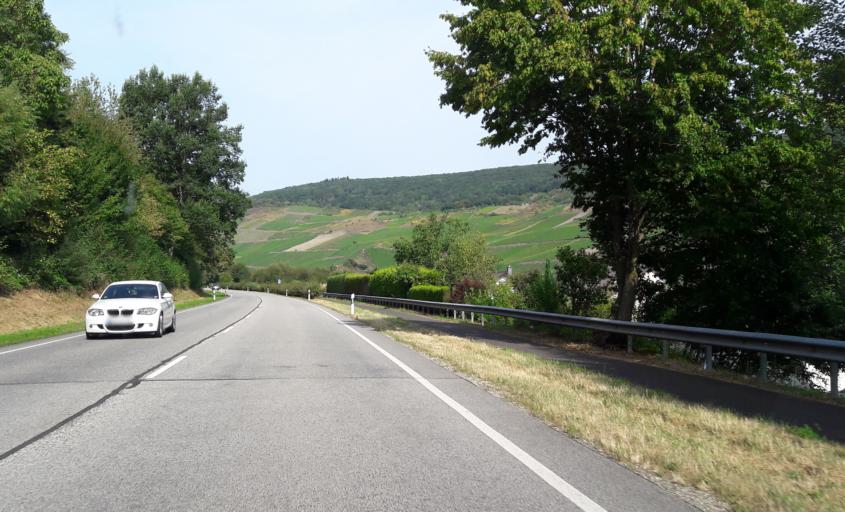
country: DE
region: Rheinland-Pfalz
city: Zell
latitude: 50.0350
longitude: 7.1699
